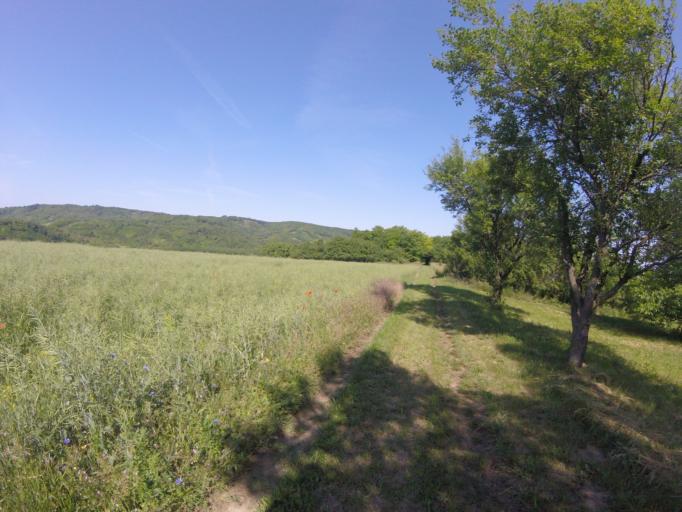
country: HU
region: Zala
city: Zalaszentgrot
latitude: 46.9054
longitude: 17.0627
